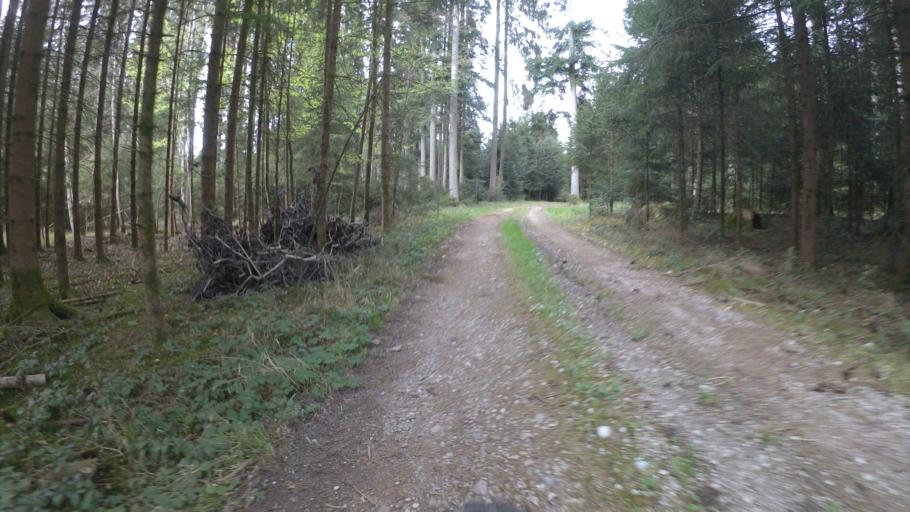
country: DE
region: Bavaria
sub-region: Upper Bavaria
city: Nussdorf
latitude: 47.9175
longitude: 12.5835
